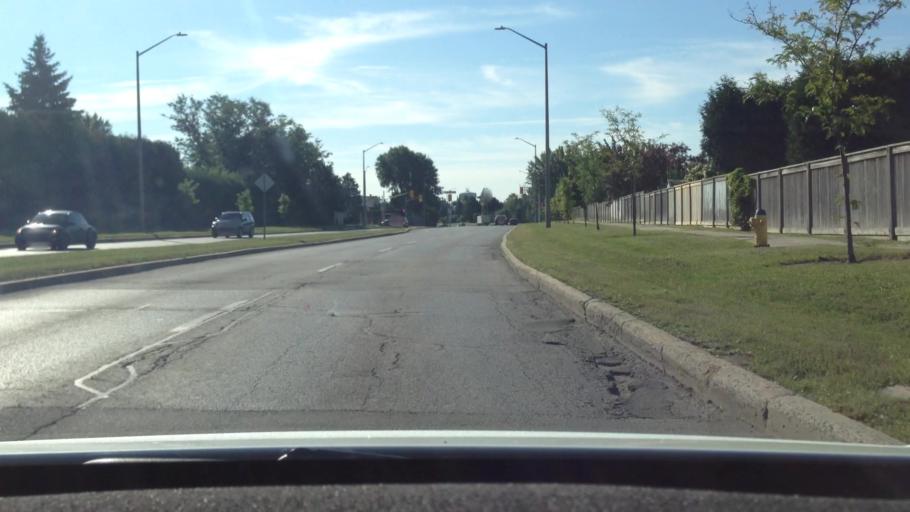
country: CA
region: Quebec
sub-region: Outaouais
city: Gatineau
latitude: 45.4616
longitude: -75.5216
